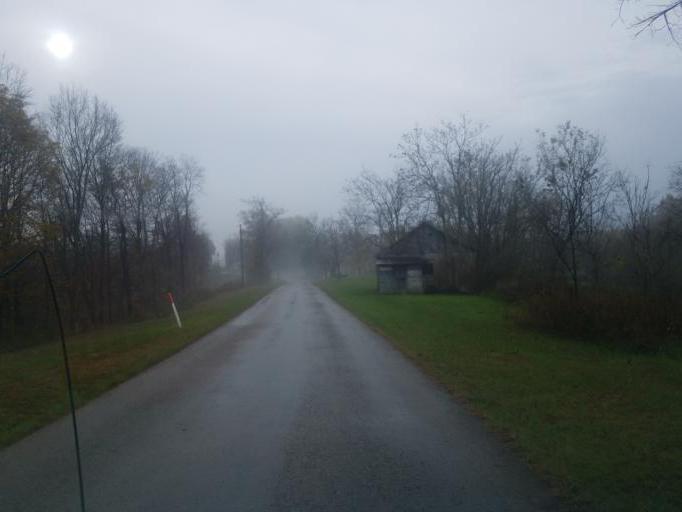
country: US
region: Ohio
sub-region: Morgan County
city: McConnelsville
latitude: 39.5045
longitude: -81.8244
